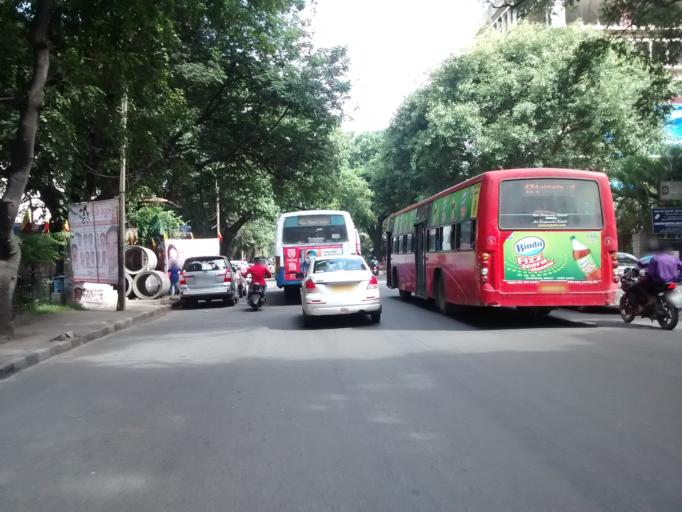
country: IN
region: Karnataka
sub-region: Bangalore Urban
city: Bangalore
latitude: 12.9730
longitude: 77.5867
